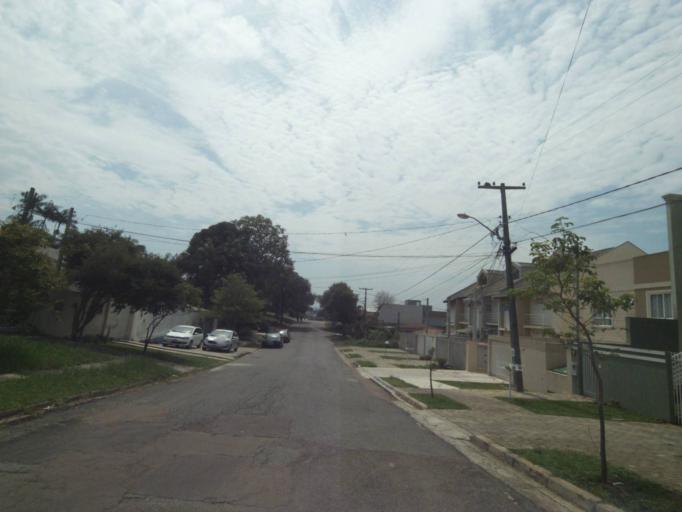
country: BR
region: Parana
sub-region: Pinhais
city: Pinhais
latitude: -25.4266
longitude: -49.2060
